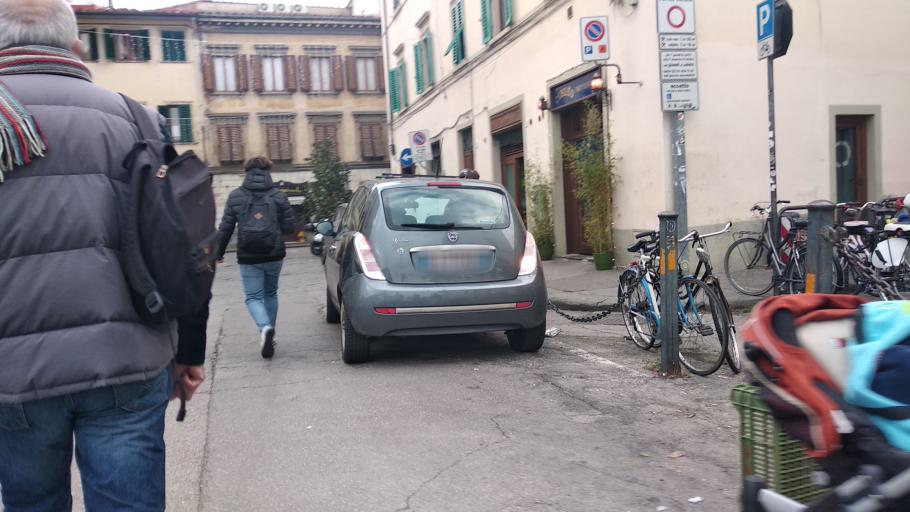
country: IT
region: Tuscany
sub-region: Province of Florence
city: Florence
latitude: 43.7709
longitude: 11.2667
